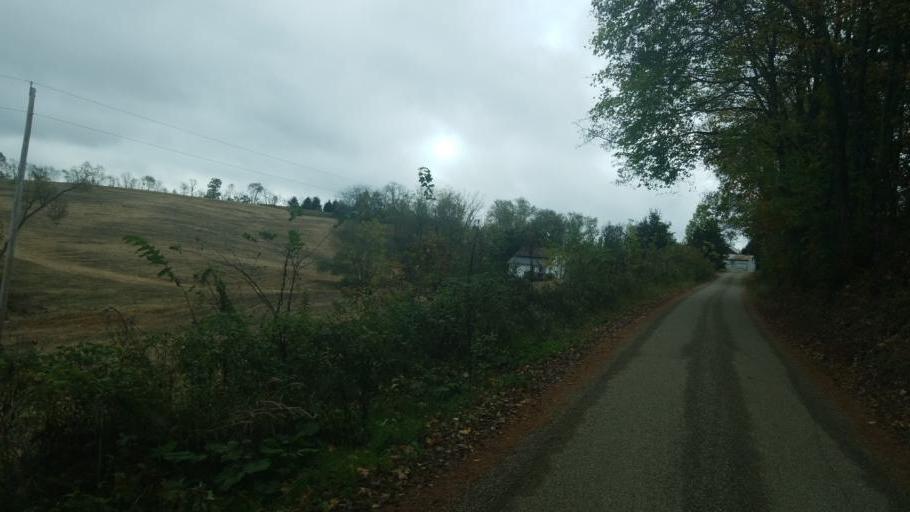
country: US
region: Ohio
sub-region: Ashland County
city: Loudonville
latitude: 40.6059
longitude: -82.1876
